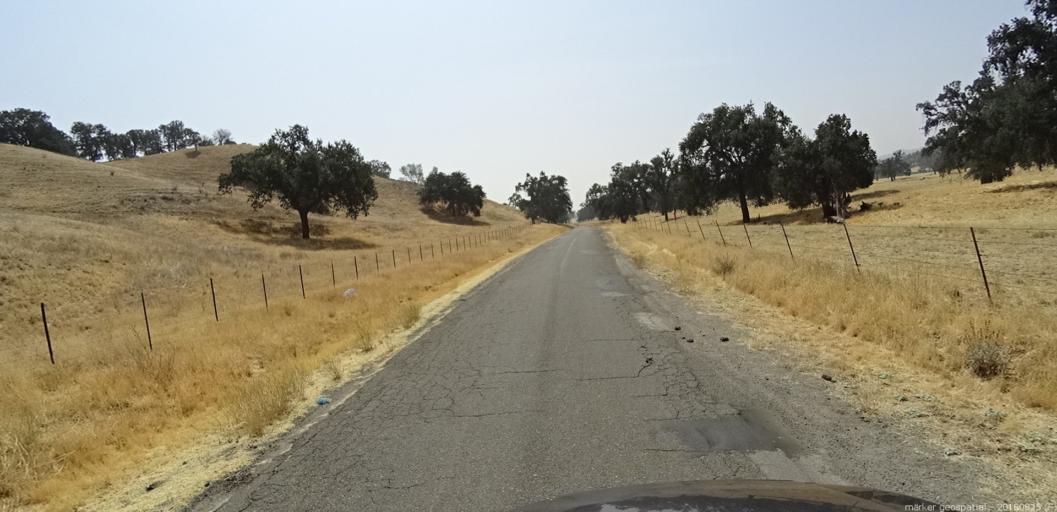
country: US
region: California
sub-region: San Luis Obispo County
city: Shandon
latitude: 35.8829
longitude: -120.4242
